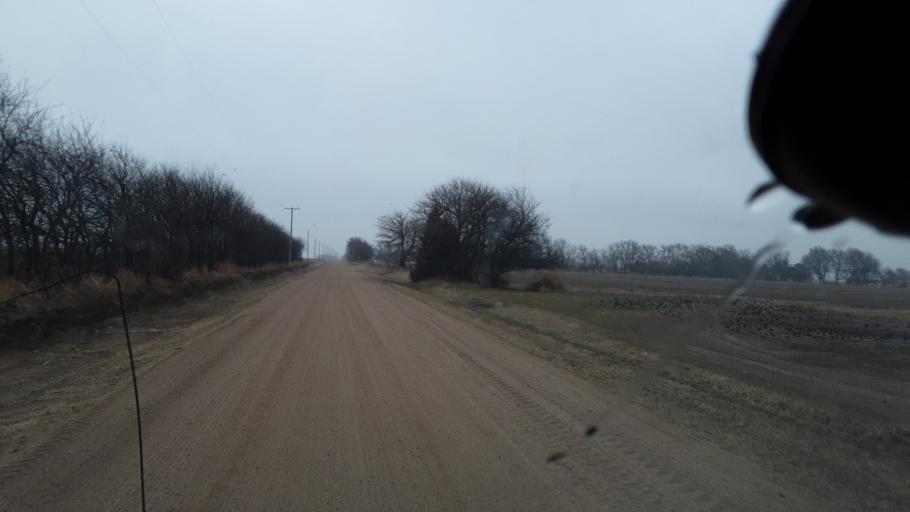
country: US
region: Kansas
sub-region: Reno County
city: South Hutchinson
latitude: 37.9555
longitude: -98.0171
